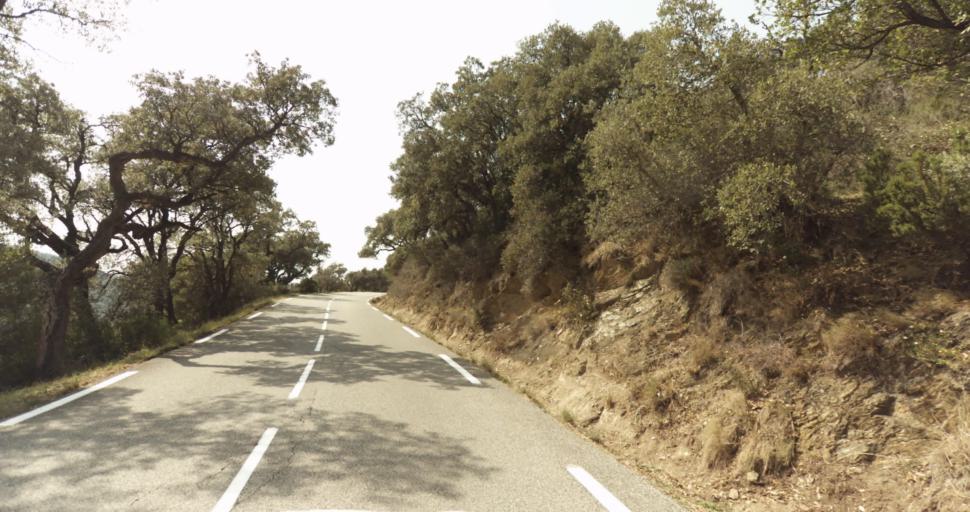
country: FR
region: Provence-Alpes-Cote d'Azur
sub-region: Departement du Var
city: Bormes-les-Mimosas
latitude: 43.1629
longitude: 6.3376
